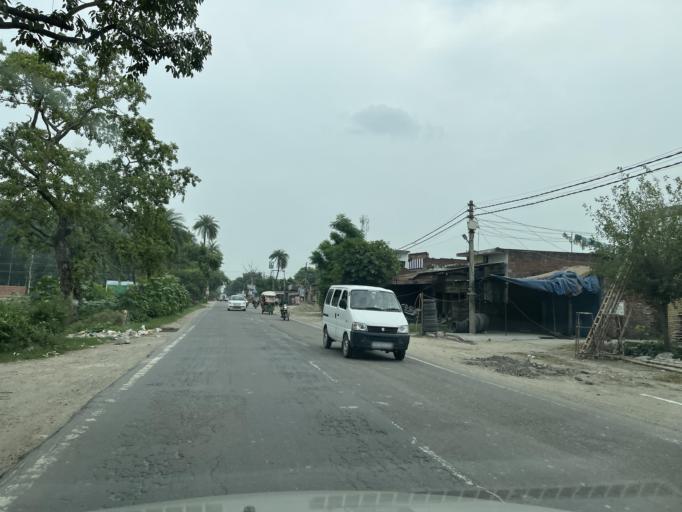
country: IN
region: Uttar Pradesh
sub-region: Rampur
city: Bilaspur
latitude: 29.0323
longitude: 79.2607
